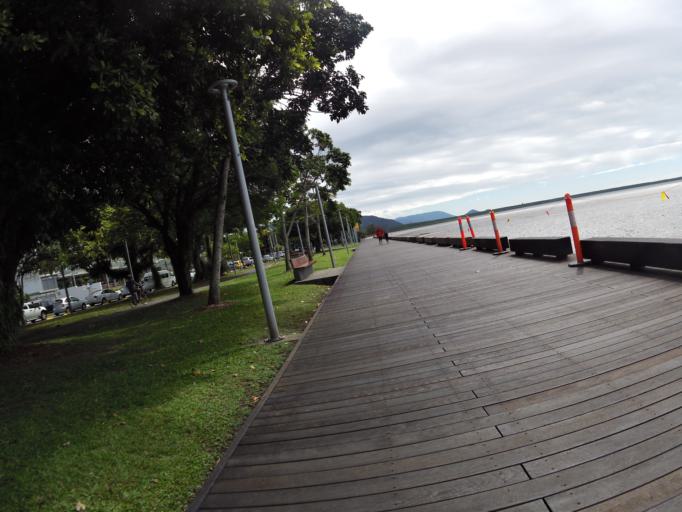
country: AU
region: Queensland
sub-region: Cairns
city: Cairns
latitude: -16.9165
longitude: 145.7747
